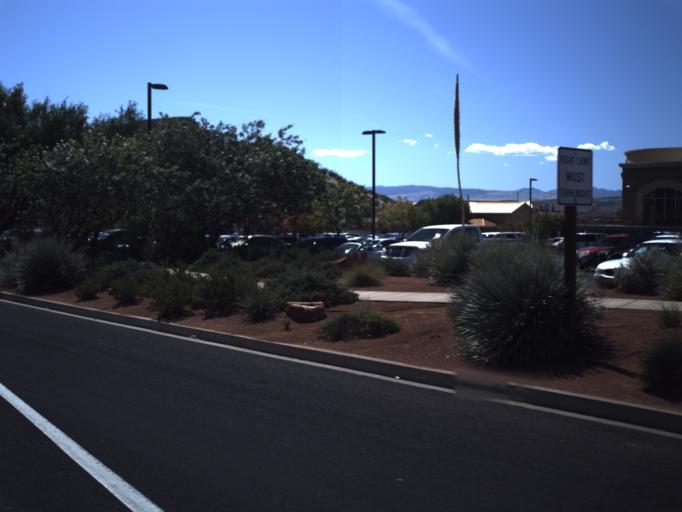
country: US
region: Utah
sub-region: Washington County
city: Saint George
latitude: 37.1262
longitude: -113.6012
